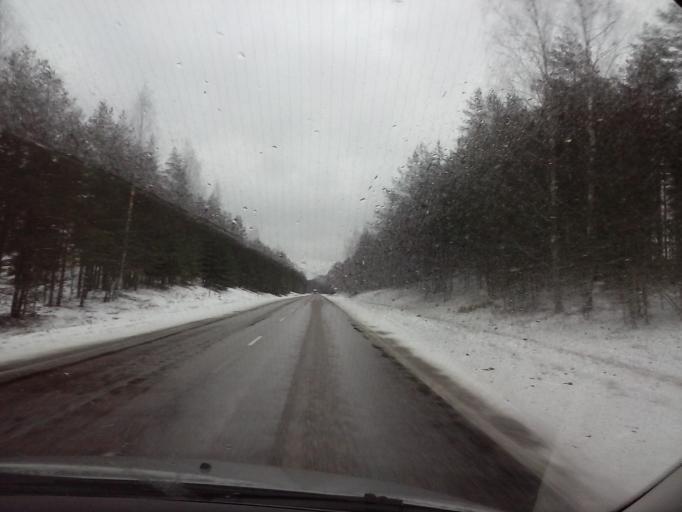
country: LV
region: Strenci
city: Seda
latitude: 57.6321
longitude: 25.8148
